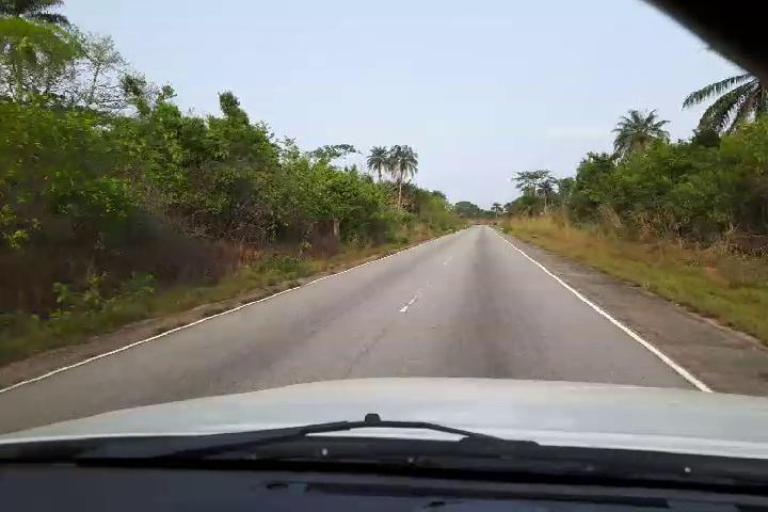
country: SL
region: Southern Province
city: Baoma
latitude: 7.9247
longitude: -11.5366
